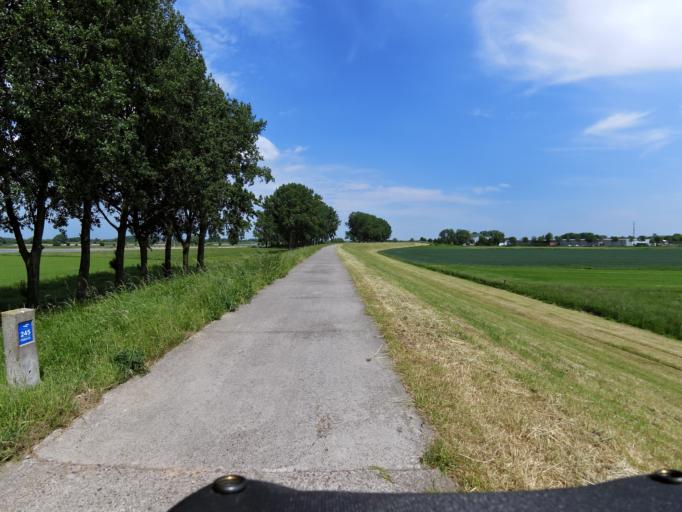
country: NL
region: North Brabant
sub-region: Gemeente Woudrichem
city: Woudrichem
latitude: 51.8181
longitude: 5.0725
